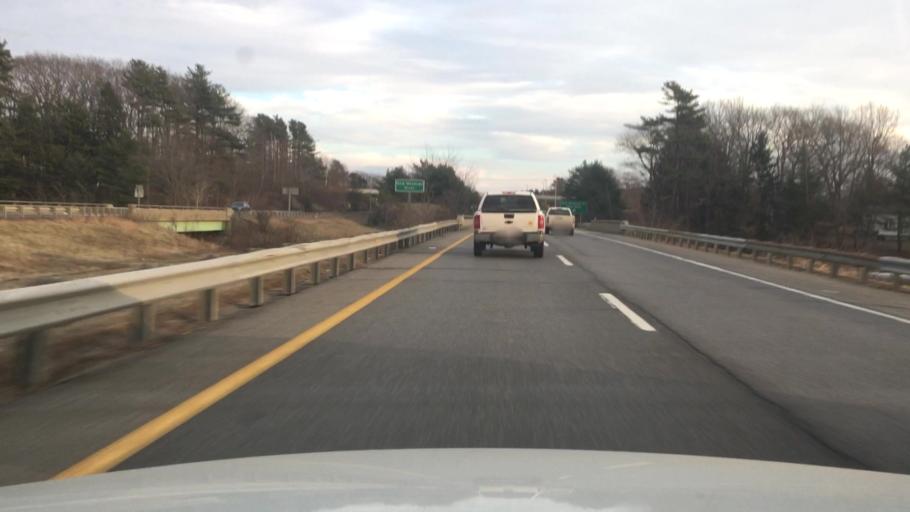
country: US
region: Maine
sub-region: Sagadahoc County
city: Bath
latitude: 43.9182
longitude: -69.8658
